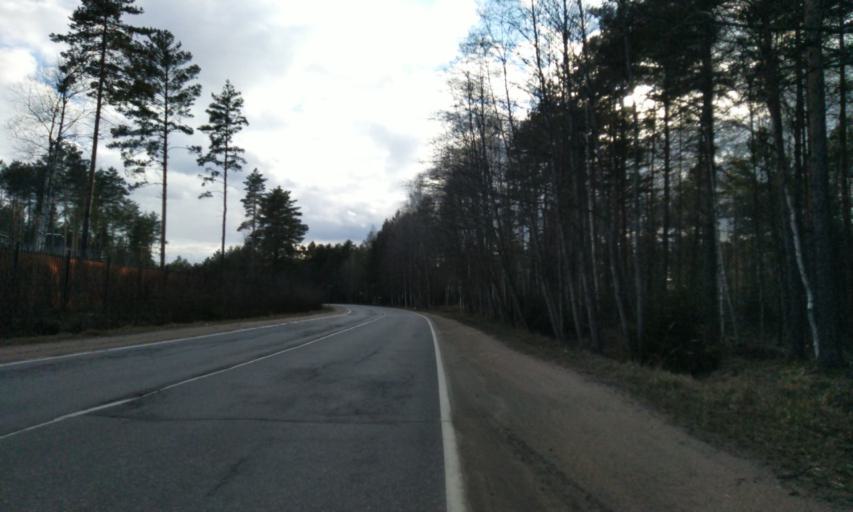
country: RU
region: Leningrad
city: Novoye Devyatkino
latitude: 60.1229
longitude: 30.4523
